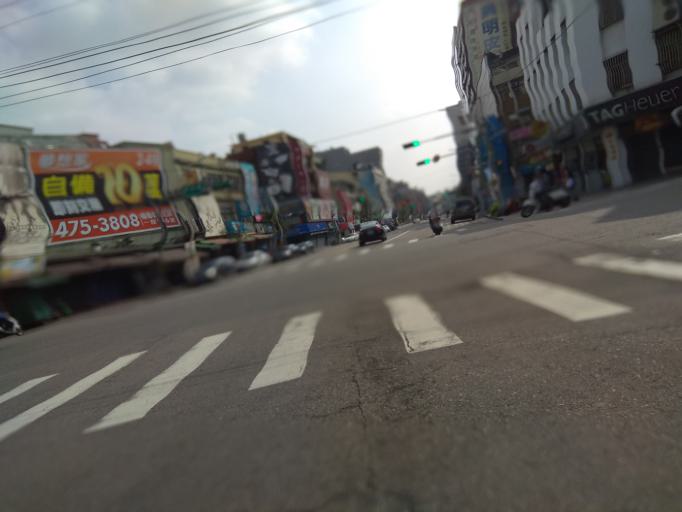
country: TW
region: Taiwan
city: Taoyuan City
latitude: 24.9578
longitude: 121.2222
